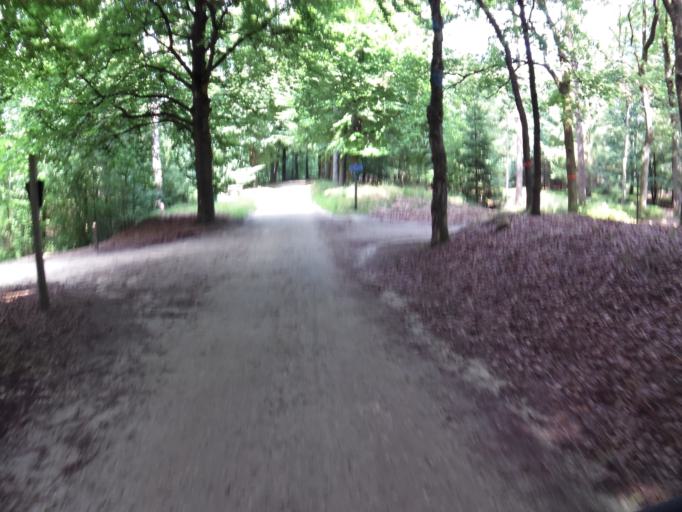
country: NL
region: Gelderland
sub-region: Gemeente Apeldoorn
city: Loenen
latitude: 52.1271
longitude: 5.9980
